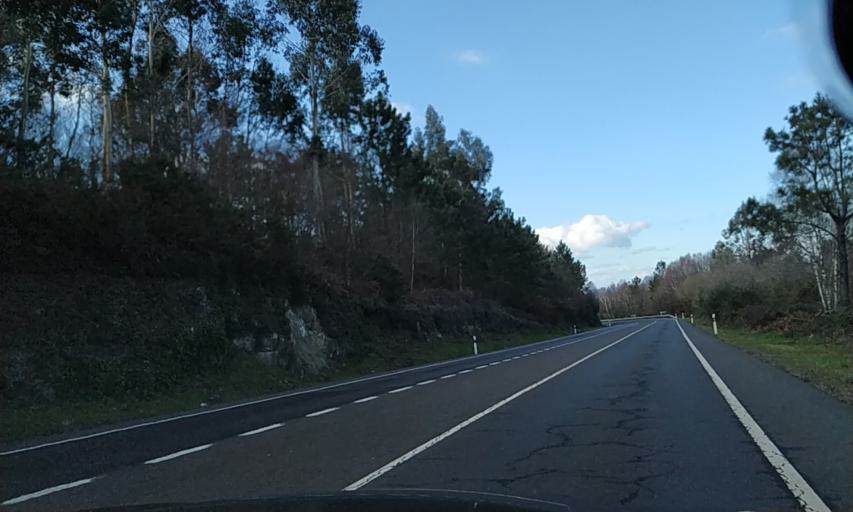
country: ES
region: Galicia
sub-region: Provincia da Coruna
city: Ribeira
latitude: 42.7122
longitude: -8.3587
